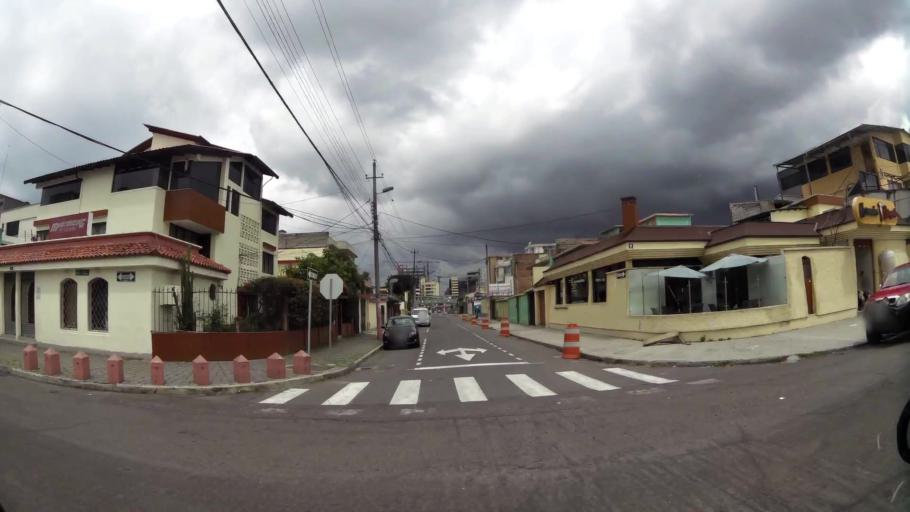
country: EC
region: Pichincha
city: Quito
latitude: -0.1673
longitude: -78.4833
